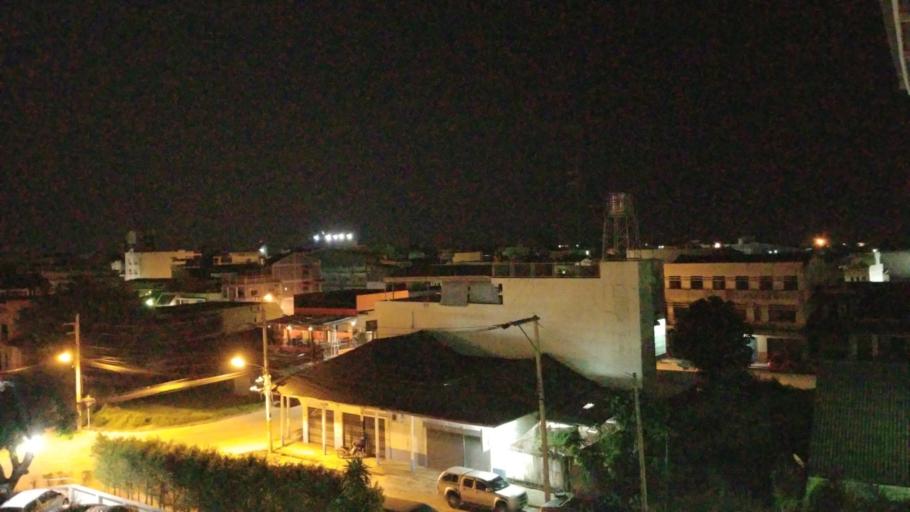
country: TH
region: Narathiwat
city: Su-ngai Kolok
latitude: 6.0217
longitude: 101.9615
